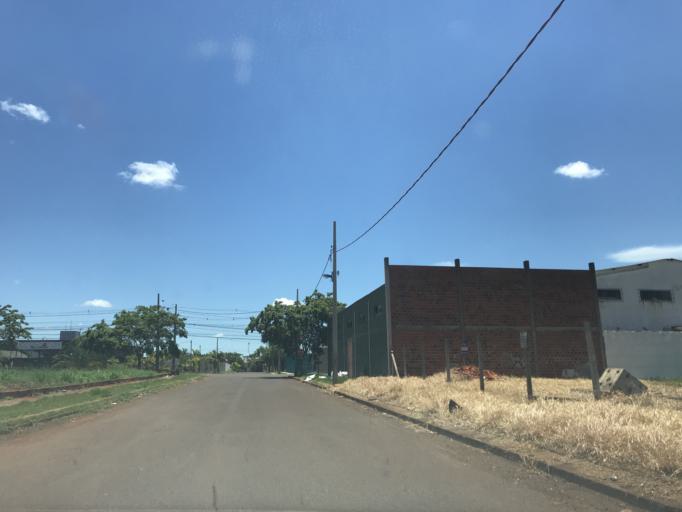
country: BR
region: Parana
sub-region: Maringa
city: Maringa
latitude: -23.4473
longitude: -51.9108
